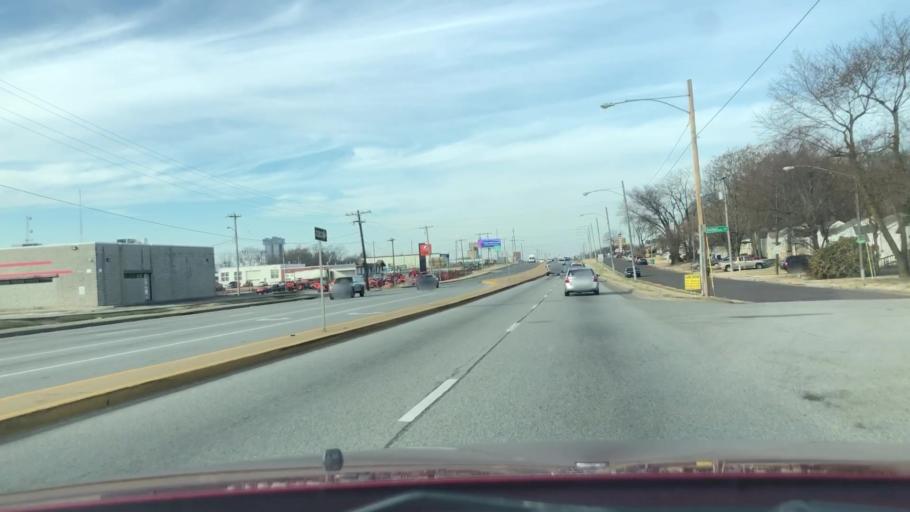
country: US
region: Missouri
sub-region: Greene County
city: Springfield
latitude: 37.2147
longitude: -93.2624
